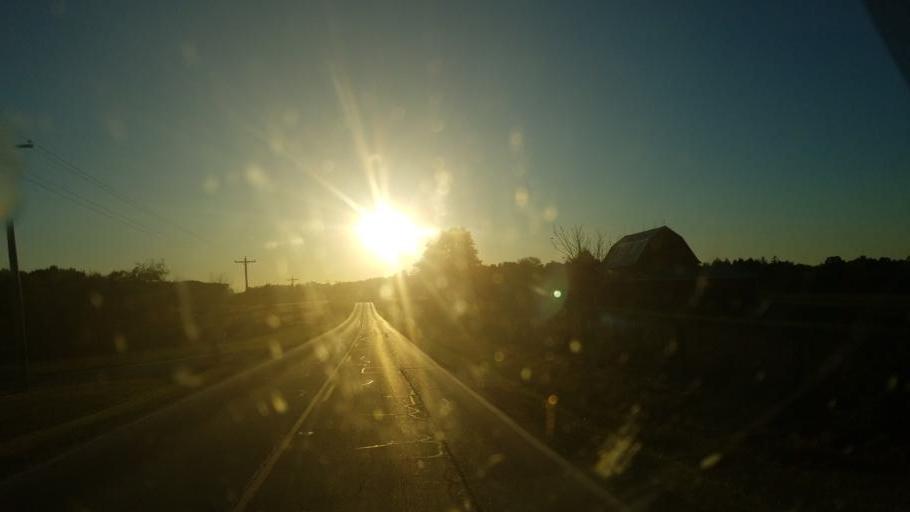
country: US
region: Ohio
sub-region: Knox County
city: Oak Hill
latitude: 40.3379
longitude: -82.2055
